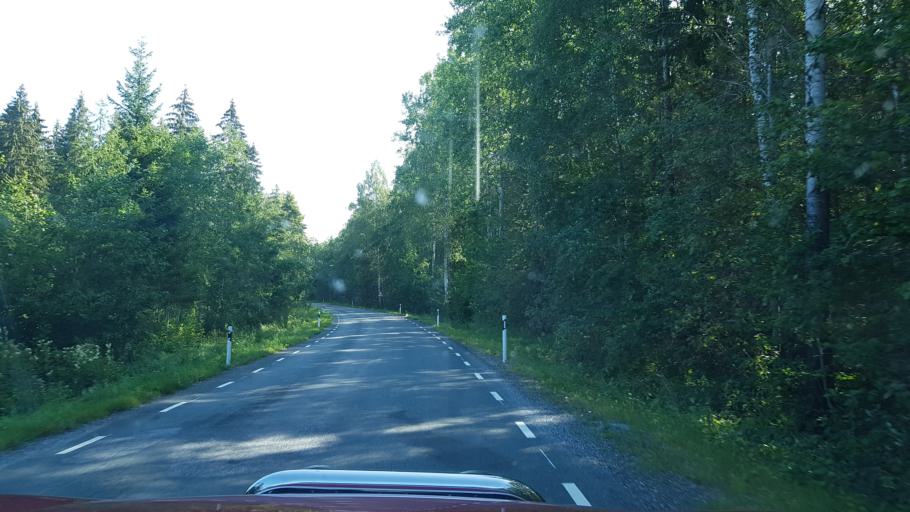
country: EE
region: Harju
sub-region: Rae vald
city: Vaida
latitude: 59.2595
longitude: 25.0589
